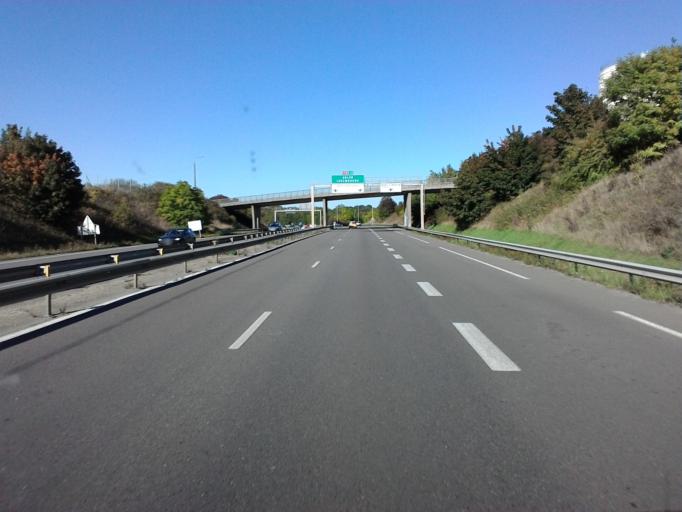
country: FR
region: Lorraine
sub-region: Departement de Meurthe-et-Moselle
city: Longwy
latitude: 49.5300
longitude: 5.7564
